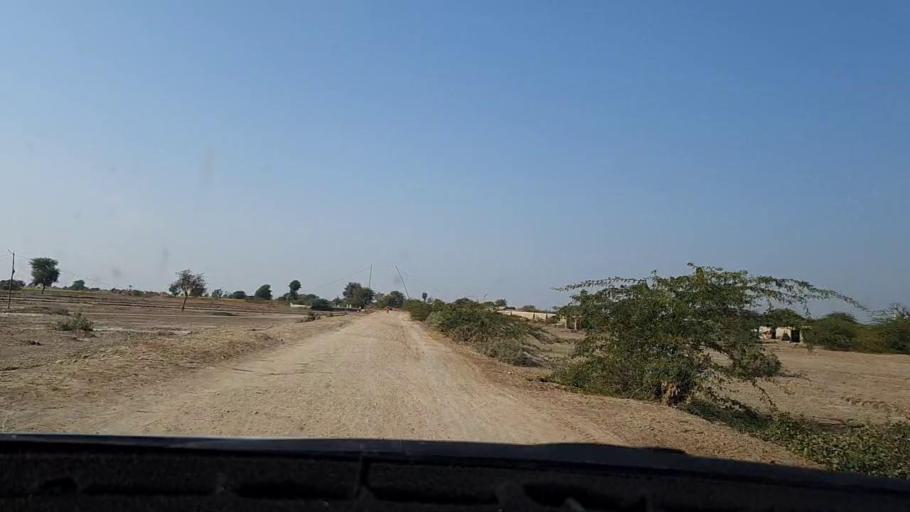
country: PK
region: Sindh
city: Tando Mittha Khan
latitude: 25.8140
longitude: 69.2901
